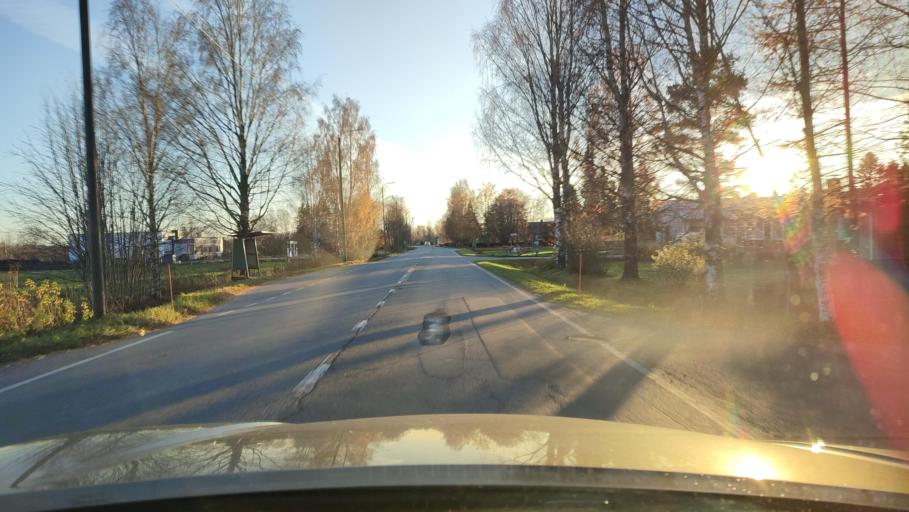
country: FI
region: Ostrobothnia
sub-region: Sydosterbotten
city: Naerpes
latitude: 62.6054
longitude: 21.4600
